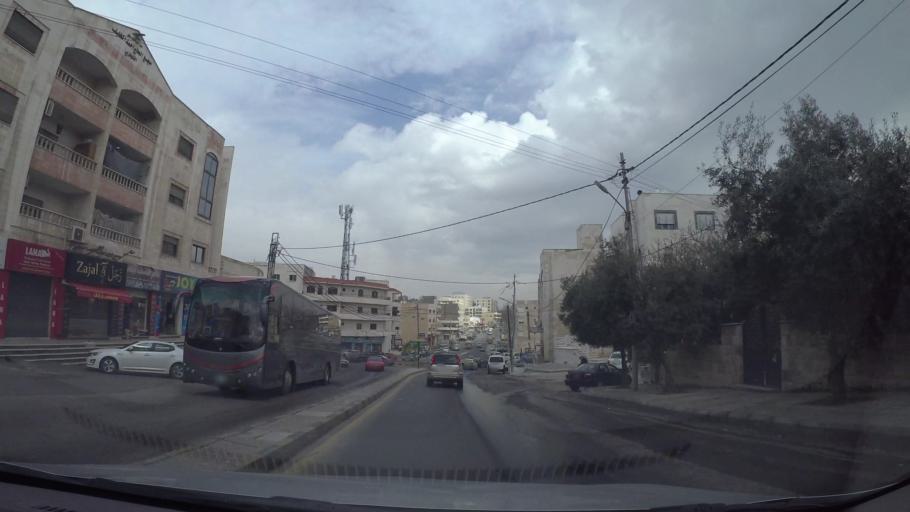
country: JO
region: Amman
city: Umm as Summaq
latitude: 31.9068
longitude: 35.8474
